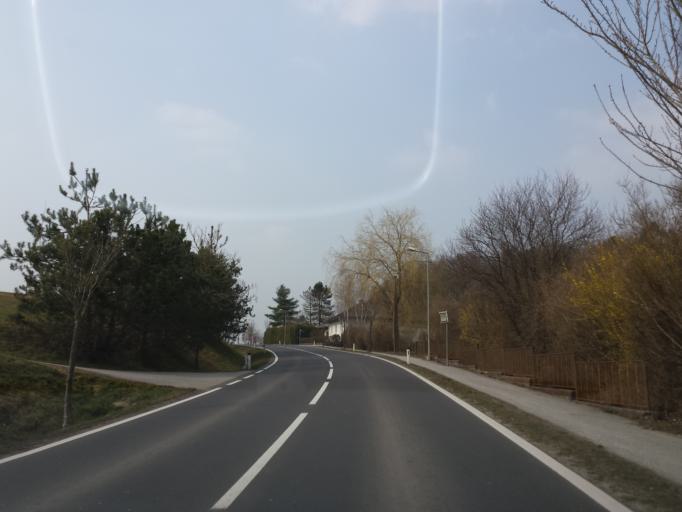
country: AT
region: Styria
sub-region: Politischer Bezirk Hartberg-Fuerstenfeld
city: Fuerstenfeld
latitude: 47.0277
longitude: 16.0915
